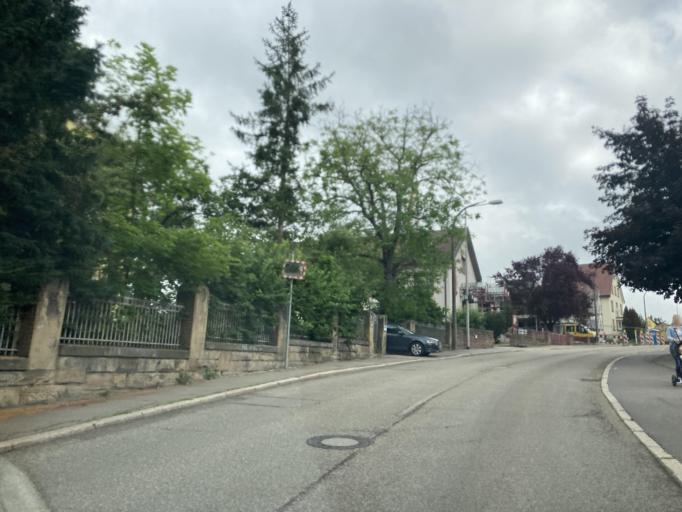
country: DE
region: Baden-Wuerttemberg
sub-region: Karlsruhe Region
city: Bretten
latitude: 49.0374
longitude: 8.7128
